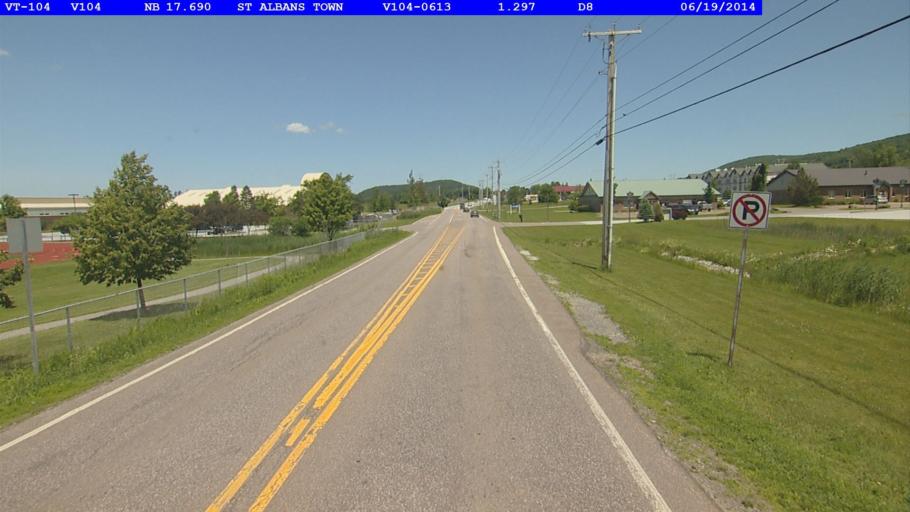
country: US
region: Vermont
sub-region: Franklin County
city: Saint Albans
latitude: 44.7920
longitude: -73.0746
